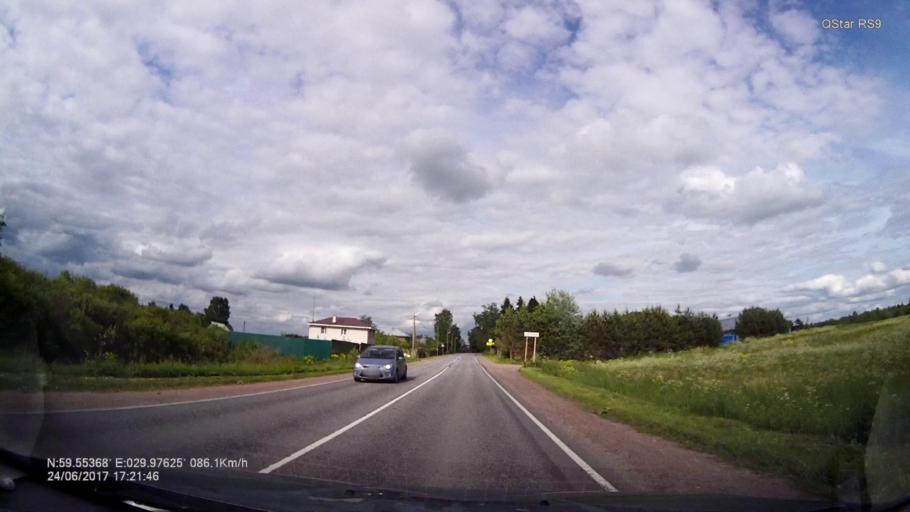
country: RU
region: Leningrad
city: Voyskovitsy
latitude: 59.5539
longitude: 29.9771
